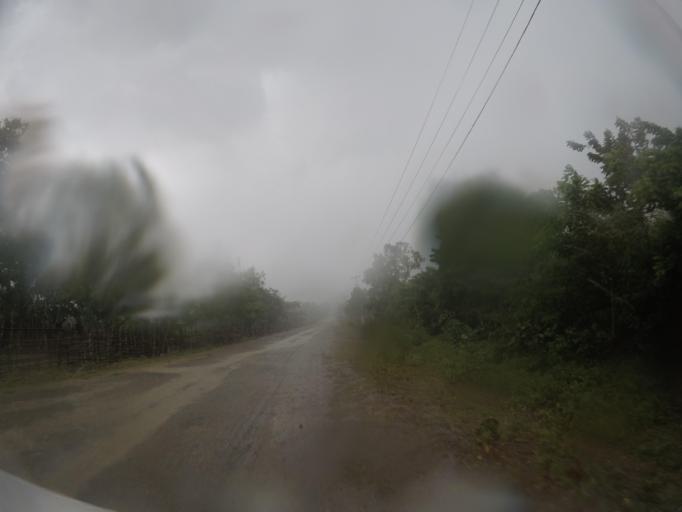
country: TL
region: Bobonaro
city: Maliana
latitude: -8.8563
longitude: 125.0957
